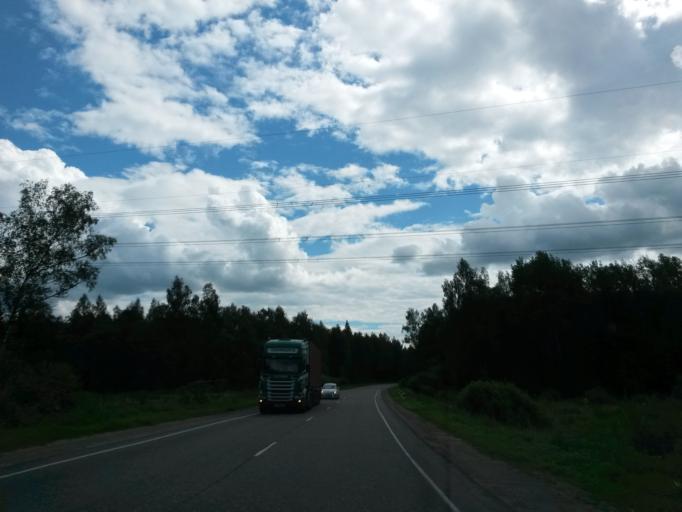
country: RU
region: Ivanovo
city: Pistsovo
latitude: 57.1167
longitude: 40.6438
